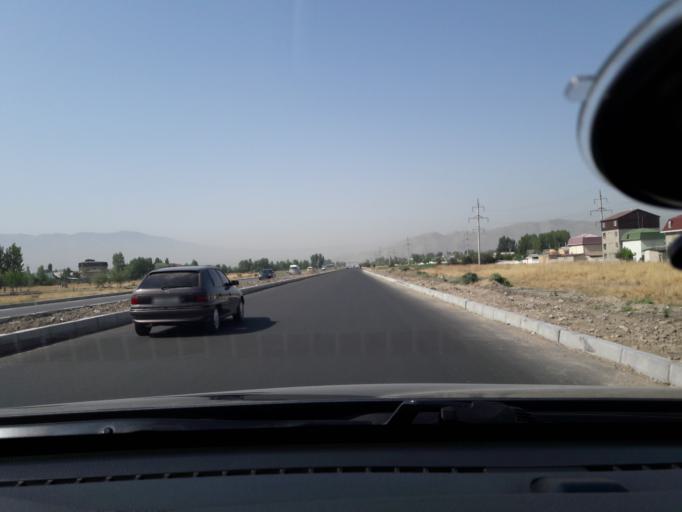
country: TJ
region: Dushanbe
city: Dushanbe
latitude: 38.4933
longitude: 68.7527
